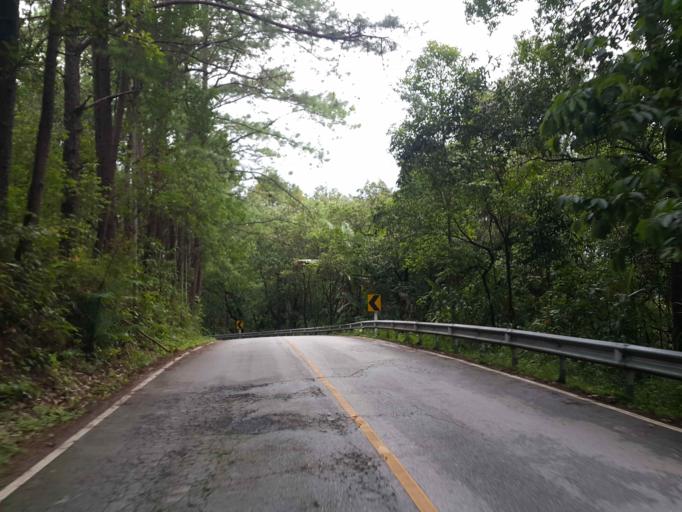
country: TH
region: Chiang Mai
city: Mae Chaem
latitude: 18.5142
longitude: 98.4556
